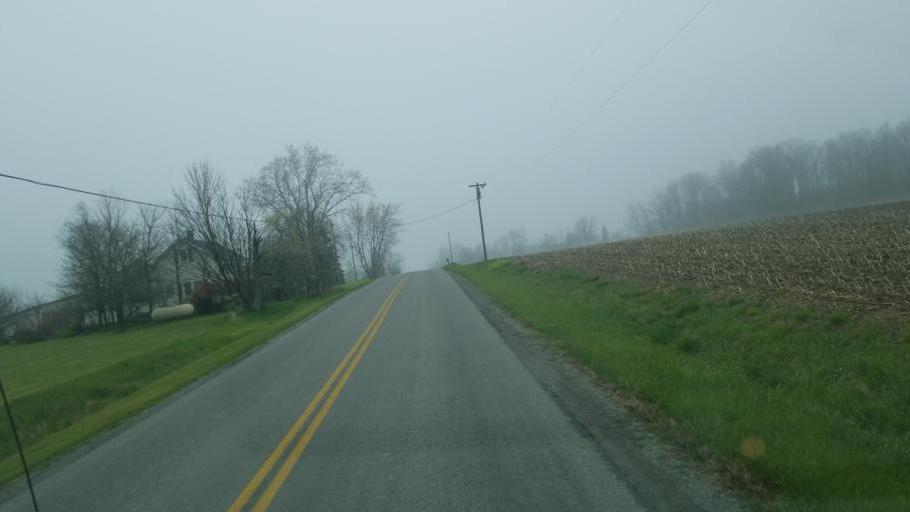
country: US
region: Ohio
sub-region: Logan County
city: De Graff
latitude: 40.3277
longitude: -83.9206
